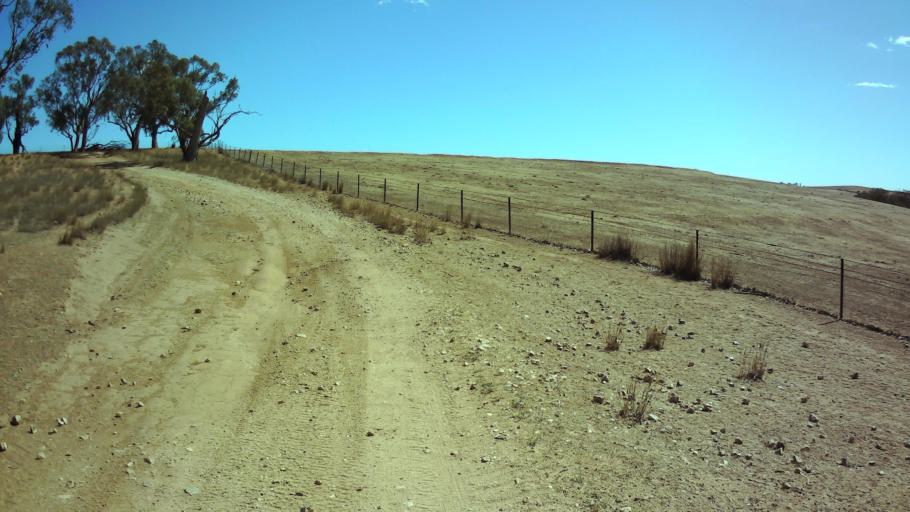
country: AU
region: New South Wales
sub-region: Weddin
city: Grenfell
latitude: -33.9973
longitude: 148.4372
